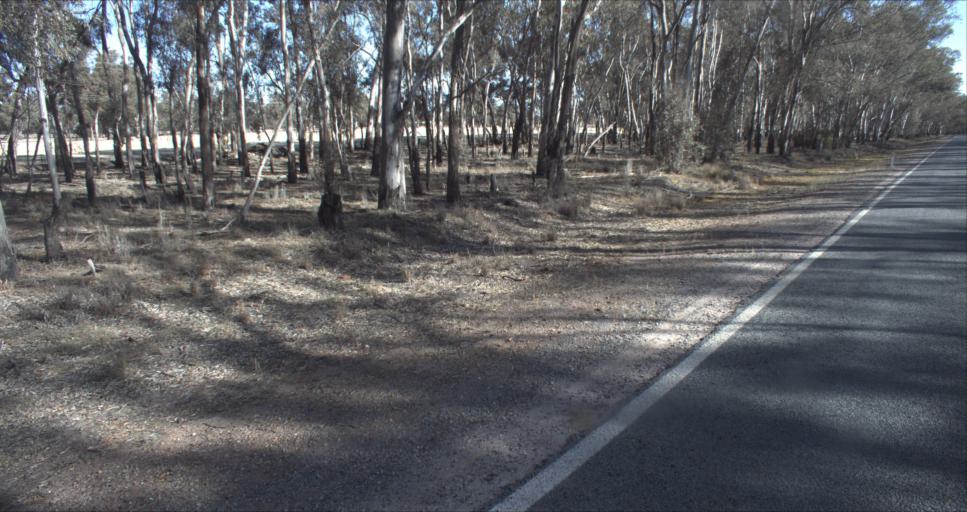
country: AU
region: New South Wales
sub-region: Leeton
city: Leeton
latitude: -34.6276
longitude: 146.3782
